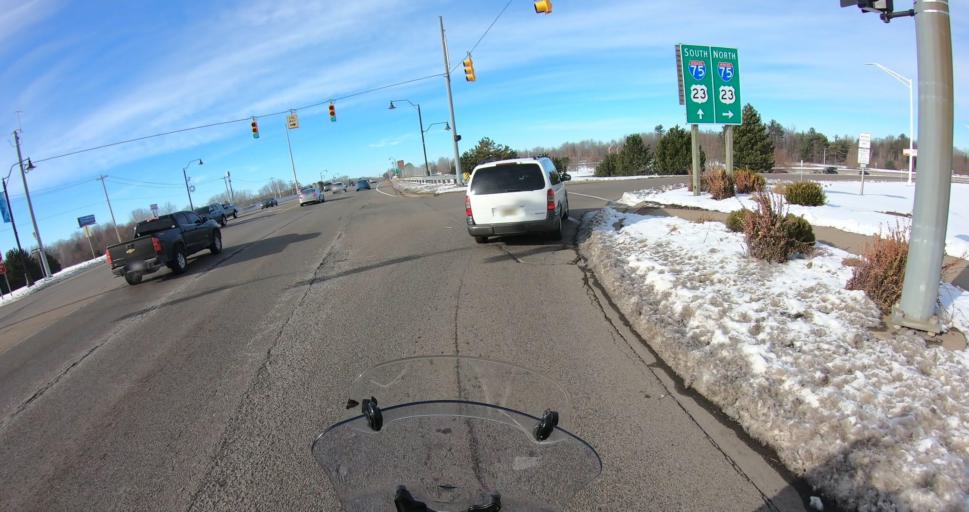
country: US
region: Michigan
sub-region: Genesee County
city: Clio
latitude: 43.1806
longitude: -83.7658
